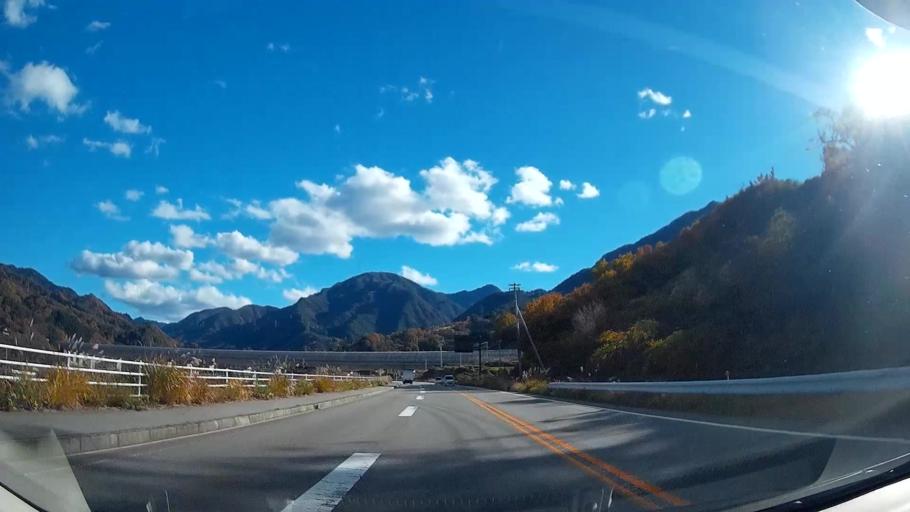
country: JP
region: Yamanashi
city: Isawa
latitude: 35.6067
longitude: 138.7027
